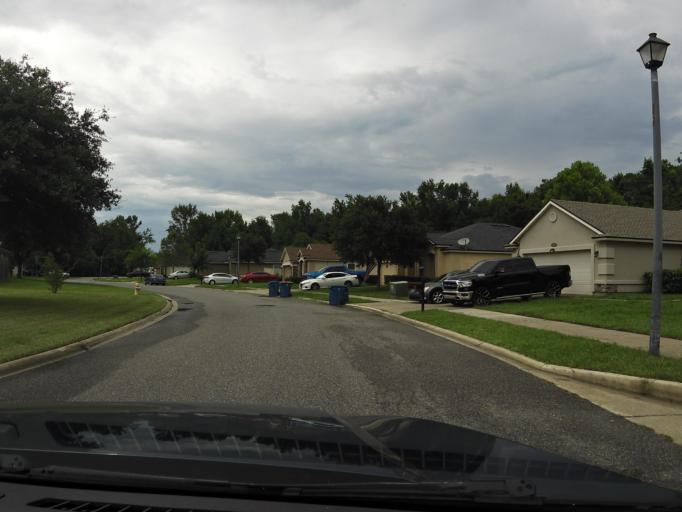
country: US
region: Florida
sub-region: Nassau County
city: Nassau Village-Ratliff
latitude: 30.4461
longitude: -81.7538
